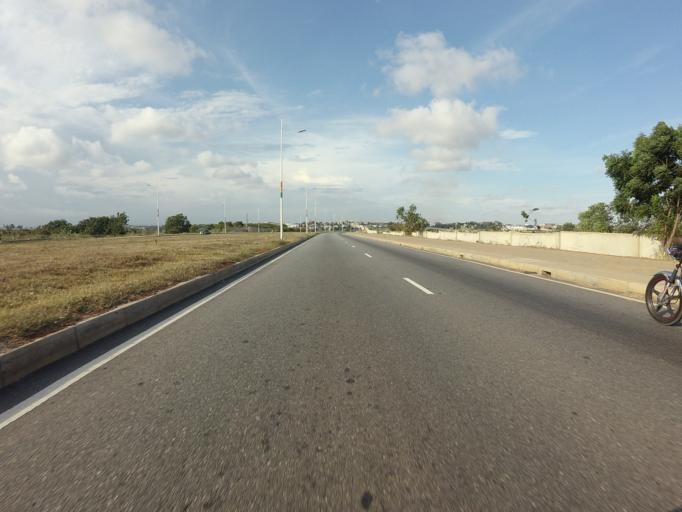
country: GH
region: Greater Accra
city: Medina Estates
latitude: 5.6113
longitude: -0.1596
